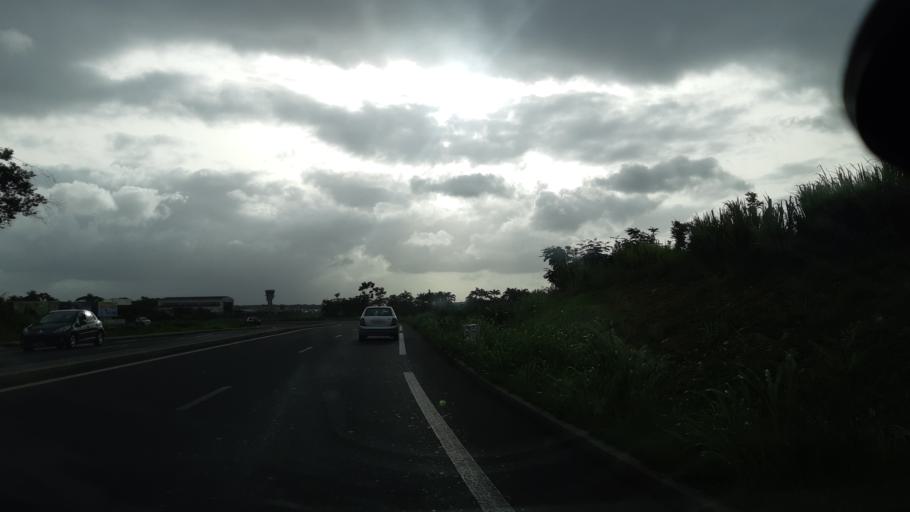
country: GP
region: Guadeloupe
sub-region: Guadeloupe
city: Les Abymes
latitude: 16.2614
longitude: -61.5146
